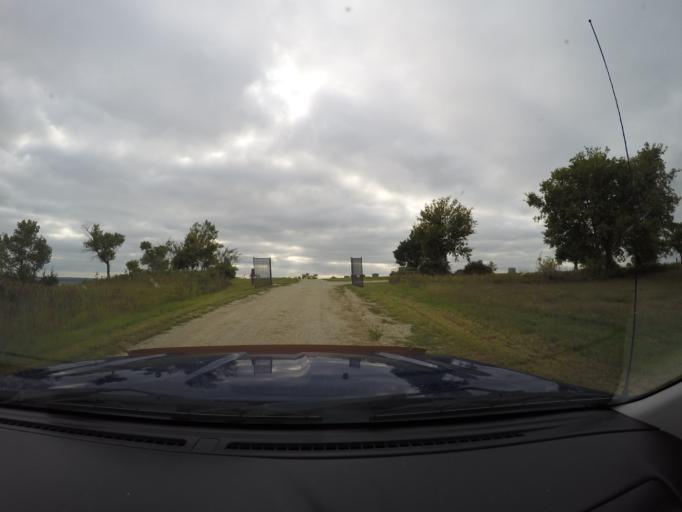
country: US
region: Kansas
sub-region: Geary County
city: Grandview Plaza
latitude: 39.0613
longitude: -96.7449
